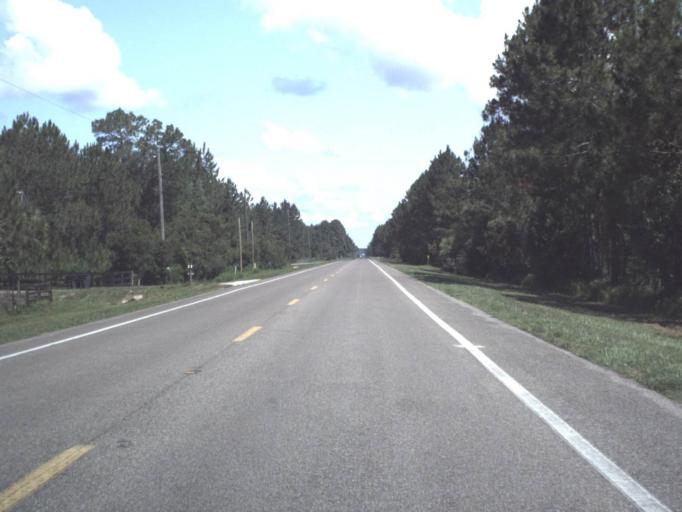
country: US
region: Florida
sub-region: Putnam County
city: East Palatka
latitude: 29.5606
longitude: -81.5408
